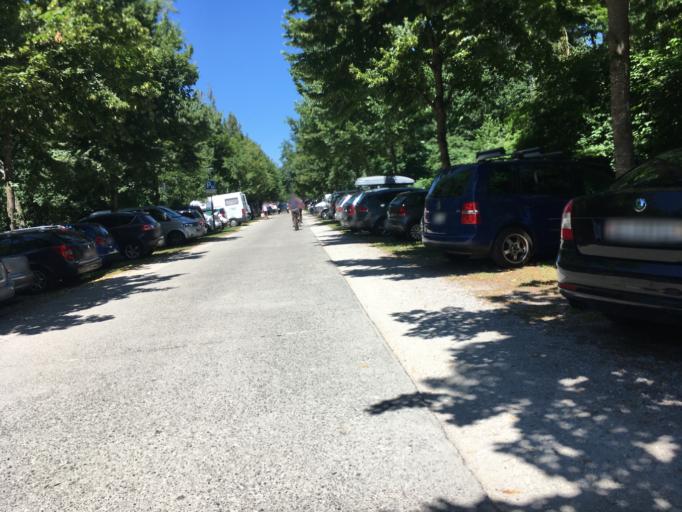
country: CH
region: Vaud
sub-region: Broye-Vully District
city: Avenches
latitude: 46.9017
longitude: 7.0495
